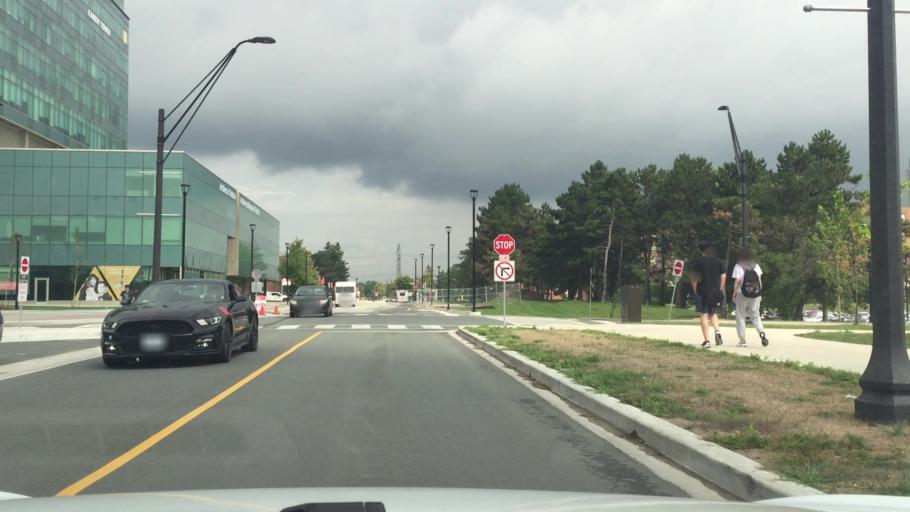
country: CA
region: Ontario
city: Concord
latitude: 43.7740
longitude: -79.4997
